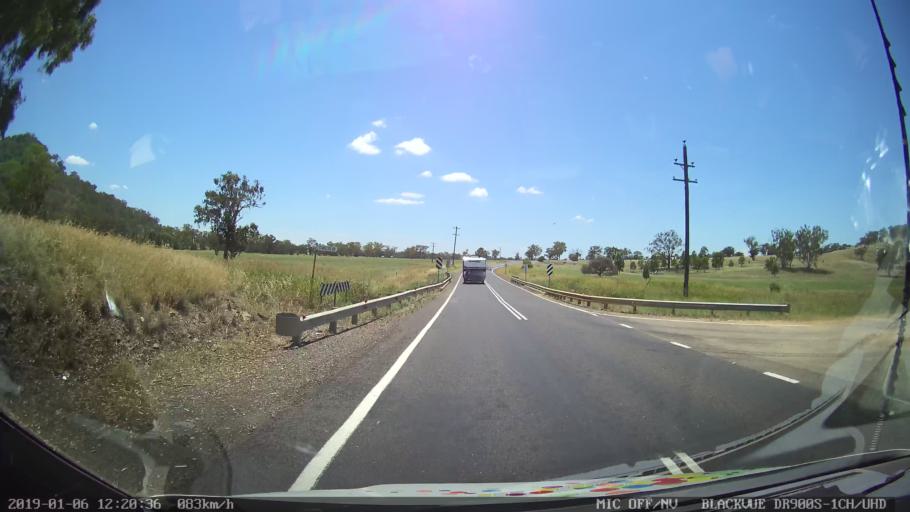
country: AU
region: New South Wales
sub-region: Tamworth Municipality
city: Phillip
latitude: -31.2759
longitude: 150.7713
